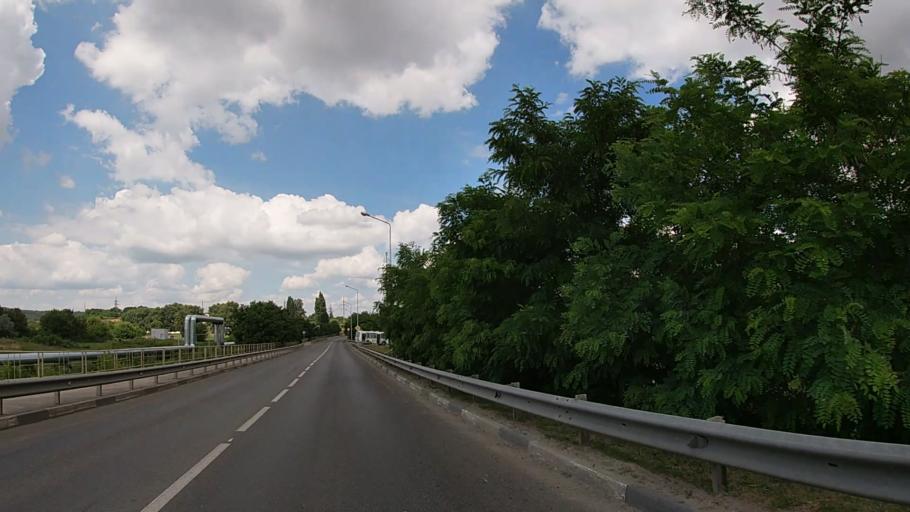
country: RU
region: Belgorod
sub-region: Belgorodskiy Rayon
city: Belgorod
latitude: 50.5915
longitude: 36.5640
